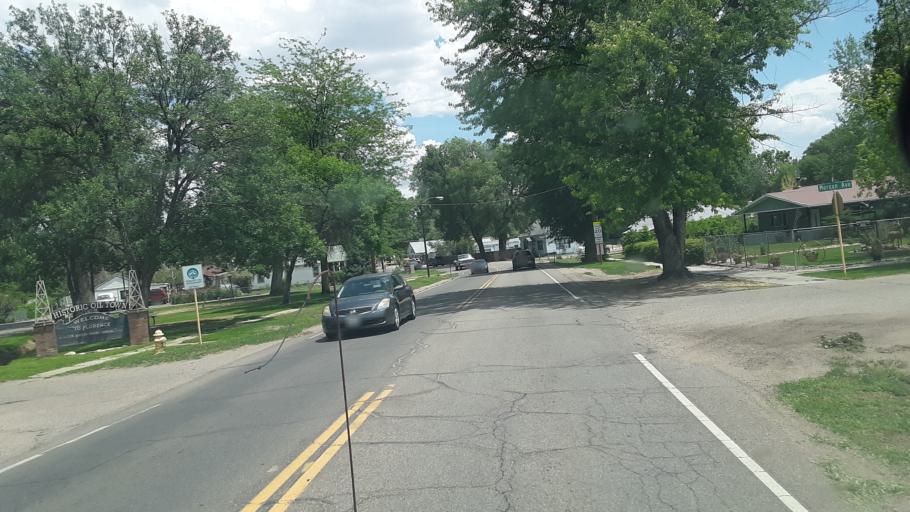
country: US
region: Colorado
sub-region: Fremont County
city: Florence
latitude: 38.3959
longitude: -105.1274
